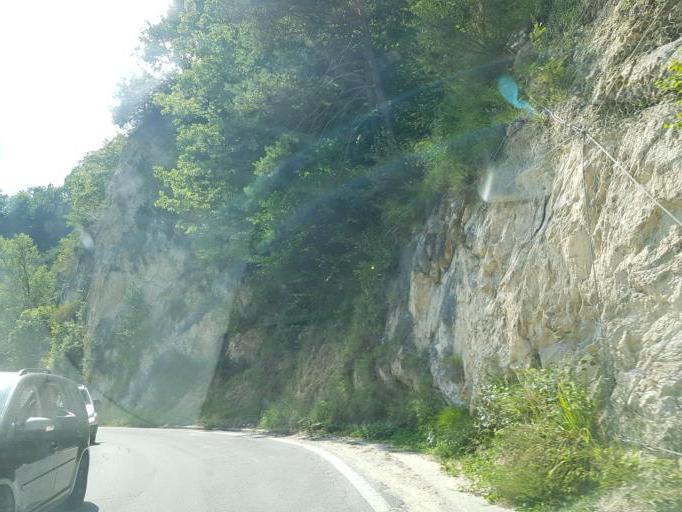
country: IT
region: Piedmont
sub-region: Provincia di Cuneo
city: Macra
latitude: 44.5002
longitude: 7.1898
